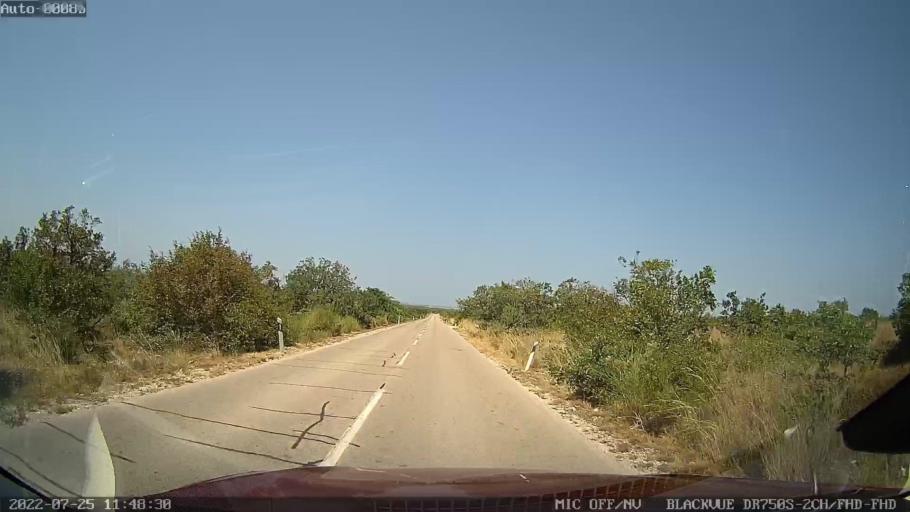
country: HR
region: Zadarska
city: Razanac
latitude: 44.2334
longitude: 15.2975
